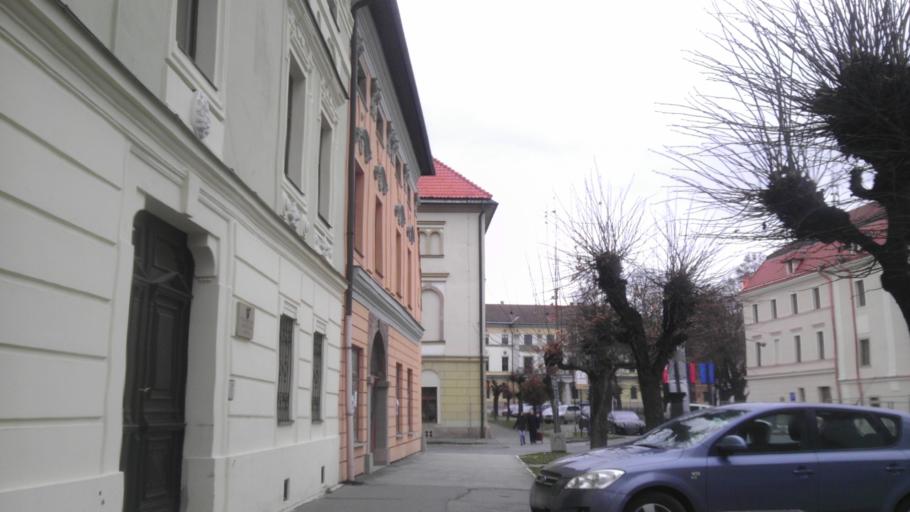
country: SK
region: Presovsky
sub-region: Okres Presov
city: Levoca
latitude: 49.0266
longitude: 20.5886
